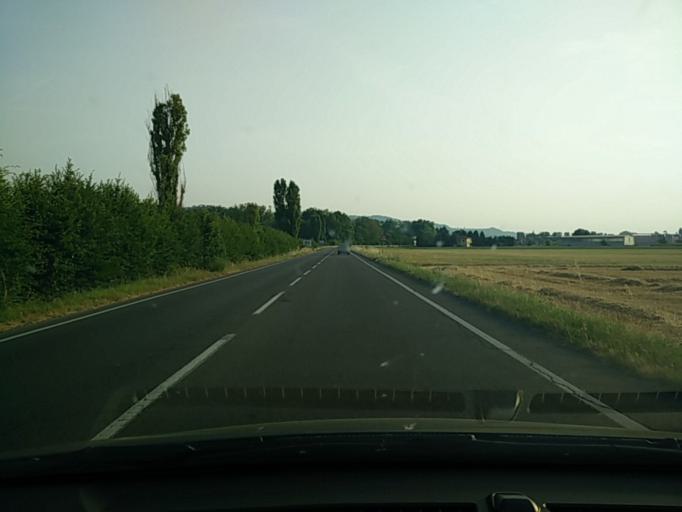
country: IT
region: Lombardy
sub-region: Provincia di Pavia
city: Cigognola
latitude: 45.0528
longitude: 9.2422
